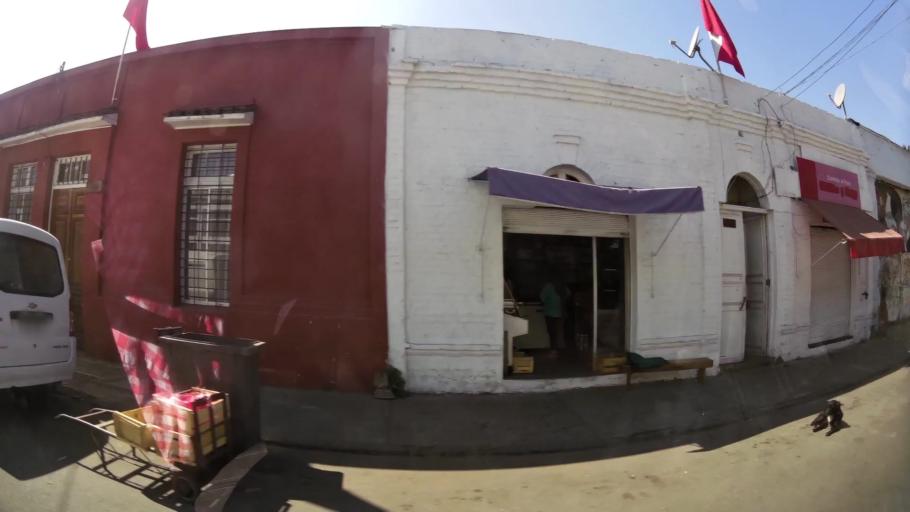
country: CL
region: Santiago Metropolitan
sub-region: Provincia de Santiago
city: Santiago
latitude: -33.4711
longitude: -70.6634
